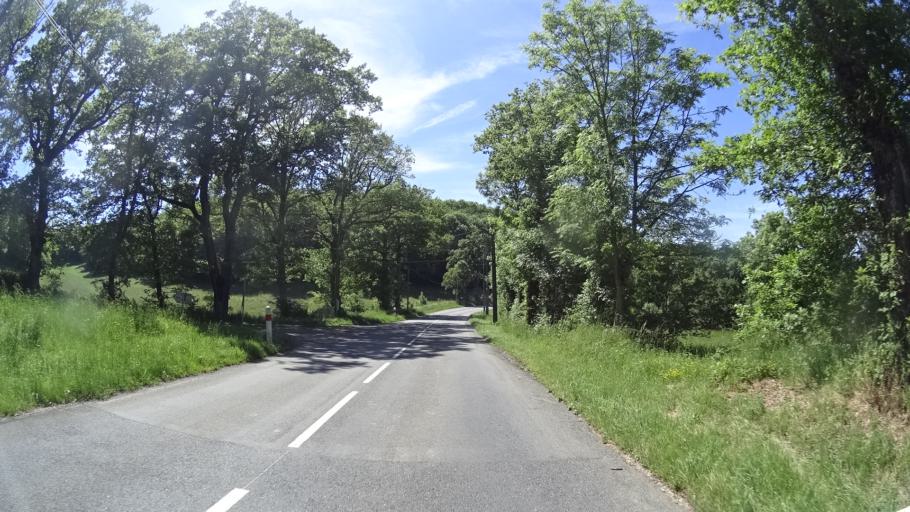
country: FR
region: Midi-Pyrenees
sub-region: Departement de l'Aveyron
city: Laissac
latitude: 44.2855
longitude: 2.8441
